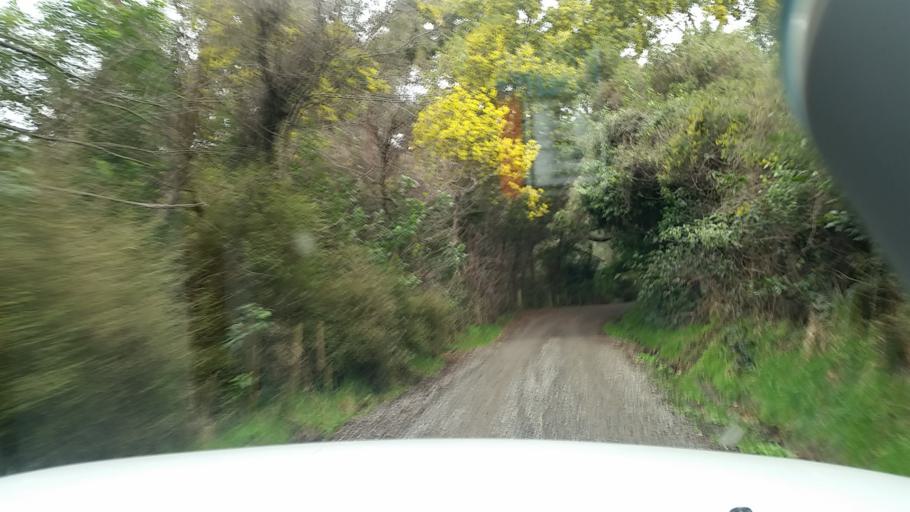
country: NZ
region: Canterbury
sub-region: Christchurch City
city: Christchurch
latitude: -43.6821
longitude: 172.7940
